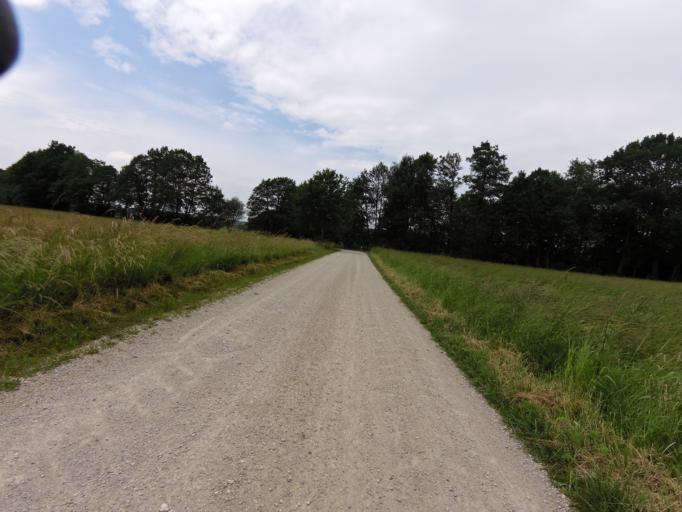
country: DE
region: Bavaria
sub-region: Upper Bavaria
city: Langenbach
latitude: 48.4556
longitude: 11.8844
